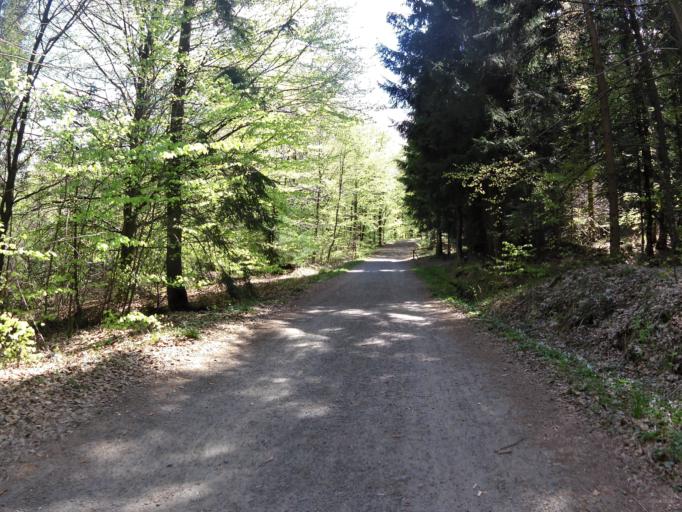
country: DE
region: Thuringia
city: Pappenheim
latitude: 50.7882
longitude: 10.5386
